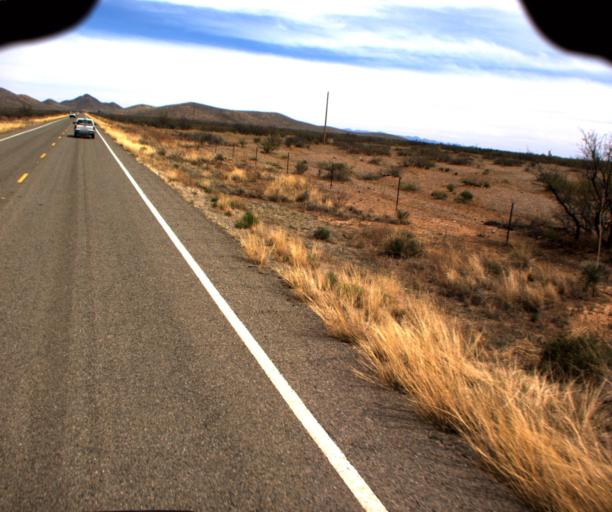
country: US
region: Arizona
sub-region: Cochise County
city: Willcox
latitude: 32.1935
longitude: -109.7033
